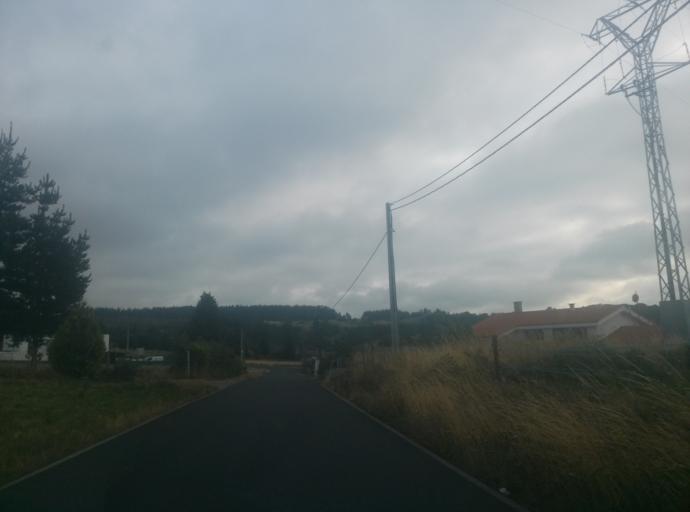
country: ES
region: Galicia
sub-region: Provincia de Lugo
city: Outeiro de Rei
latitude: 43.0862
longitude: -7.5470
